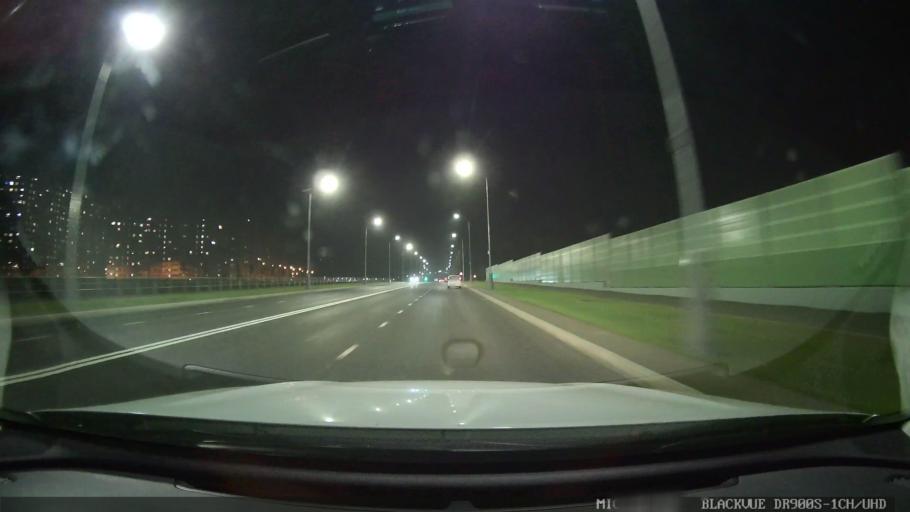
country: RU
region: Moskovskaya
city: Shcherbinka
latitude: 55.5063
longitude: 37.5384
